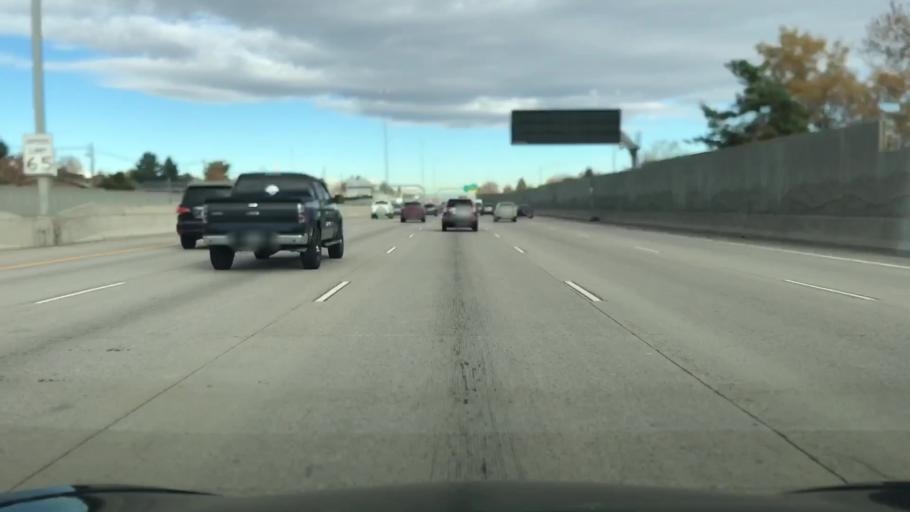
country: US
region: Colorado
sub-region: Arapahoe County
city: Greenwood Village
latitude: 39.6405
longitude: -104.9110
